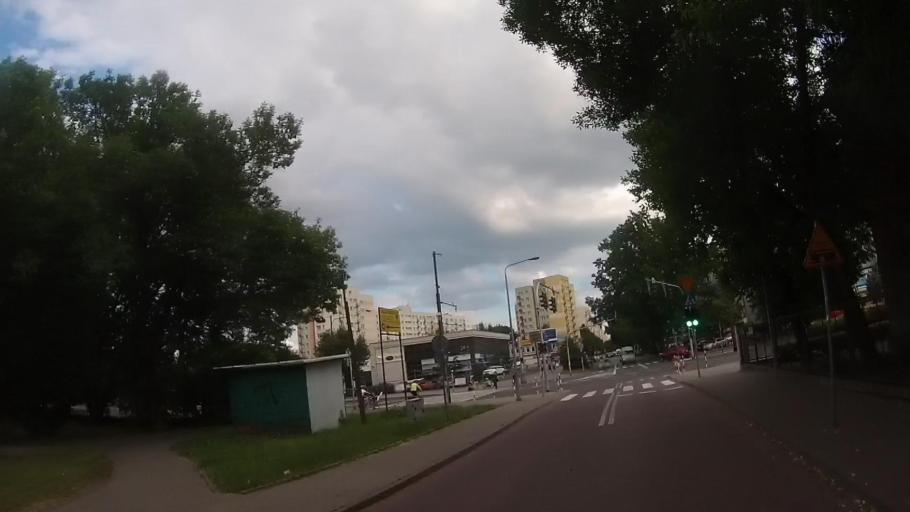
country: PL
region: Masovian Voivodeship
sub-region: Warszawa
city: Praga Poludnie
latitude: 52.2405
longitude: 21.0622
